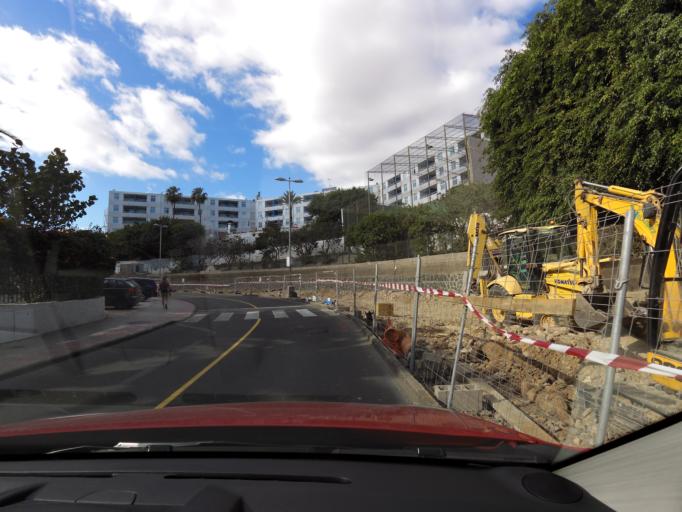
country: ES
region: Canary Islands
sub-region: Provincia de Las Palmas
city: Playa del Ingles
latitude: 27.7576
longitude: -15.5711
